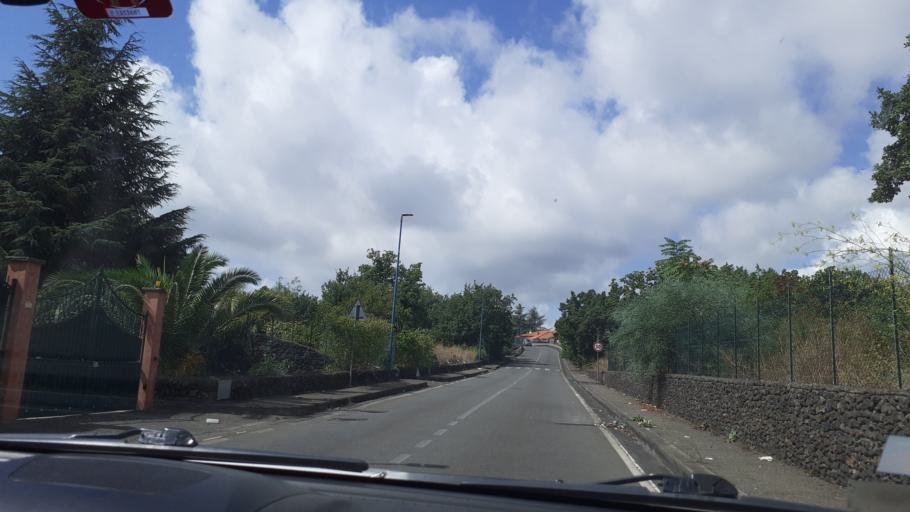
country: IT
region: Sicily
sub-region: Catania
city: Trecastagni
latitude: 37.6086
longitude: 15.0636
